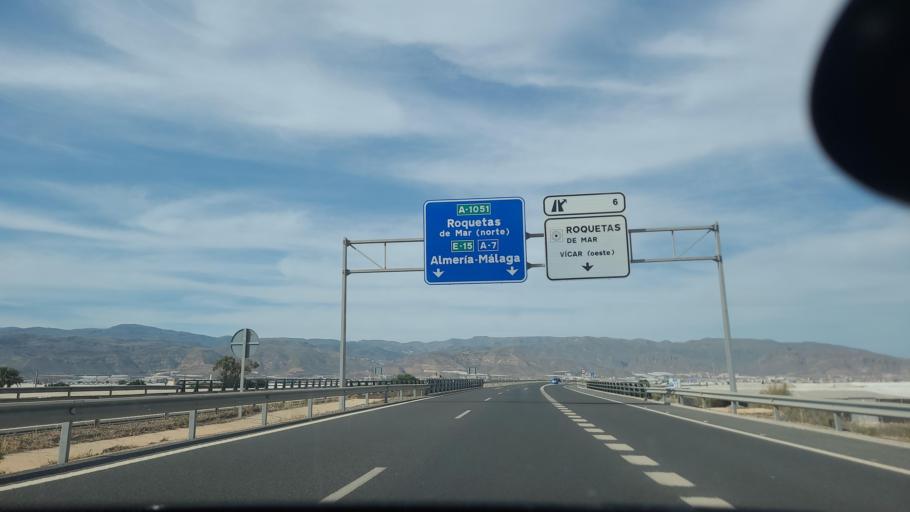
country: ES
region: Andalusia
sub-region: Provincia de Almeria
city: Roquetas de Mar
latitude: 36.7735
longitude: -2.6385
